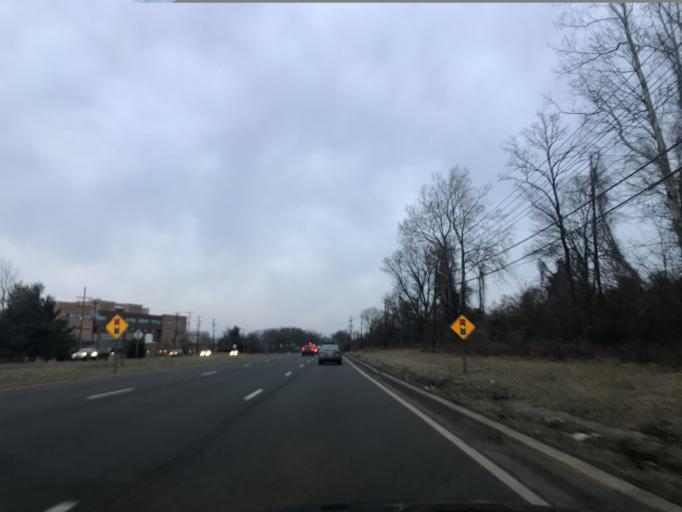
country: US
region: Maryland
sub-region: Prince George's County
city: Lake Arbor
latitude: 38.9049
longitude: -76.8337
